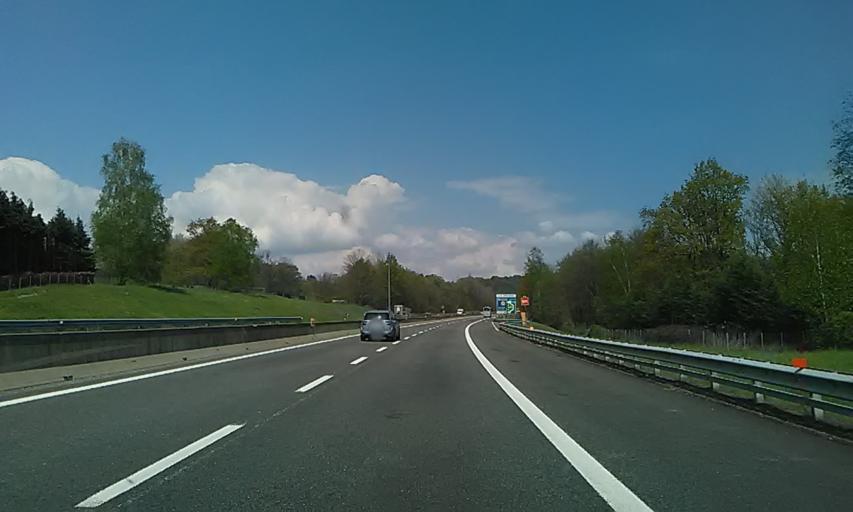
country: IT
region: Piedmont
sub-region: Provincia Verbano-Cusio-Ossola
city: Brovello
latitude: 45.8502
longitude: 8.5343
